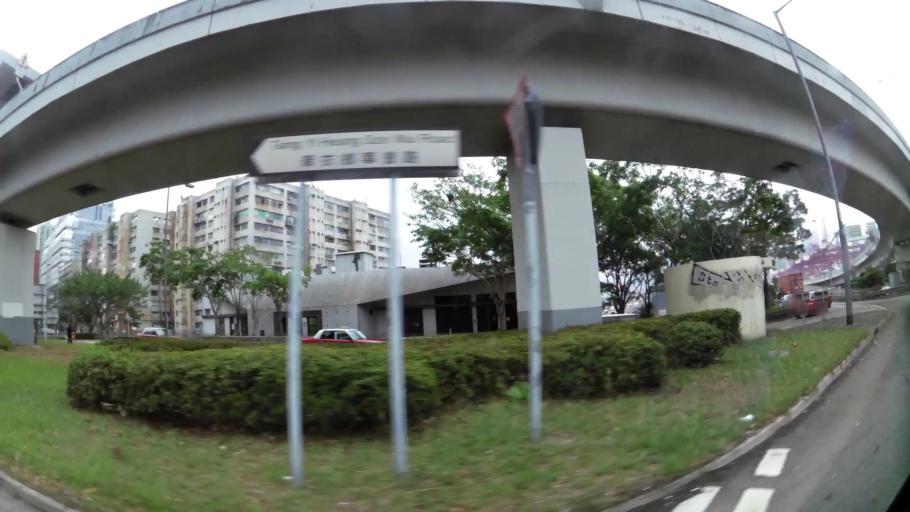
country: HK
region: Tsuen Wan
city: Tsuen Wan
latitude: 22.3479
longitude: 114.1104
